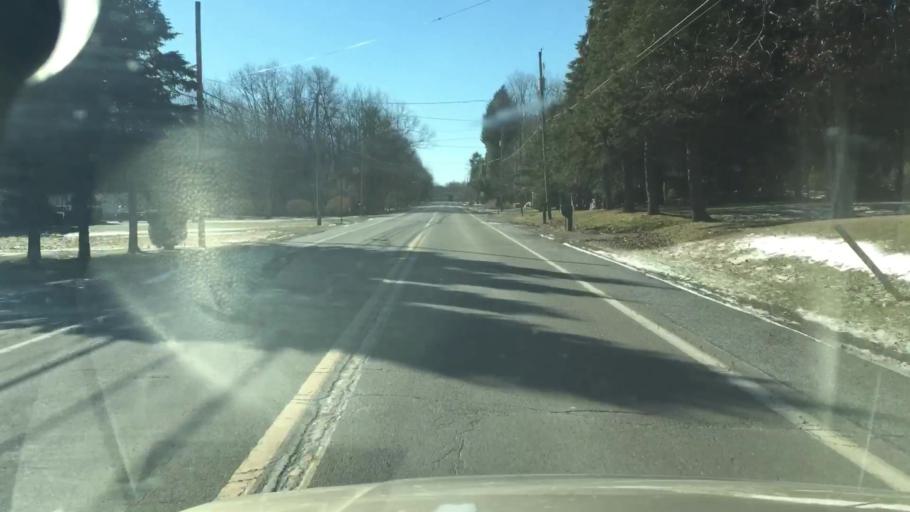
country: US
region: Pennsylvania
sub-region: Luzerne County
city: Freeland
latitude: 41.0238
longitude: -75.8705
